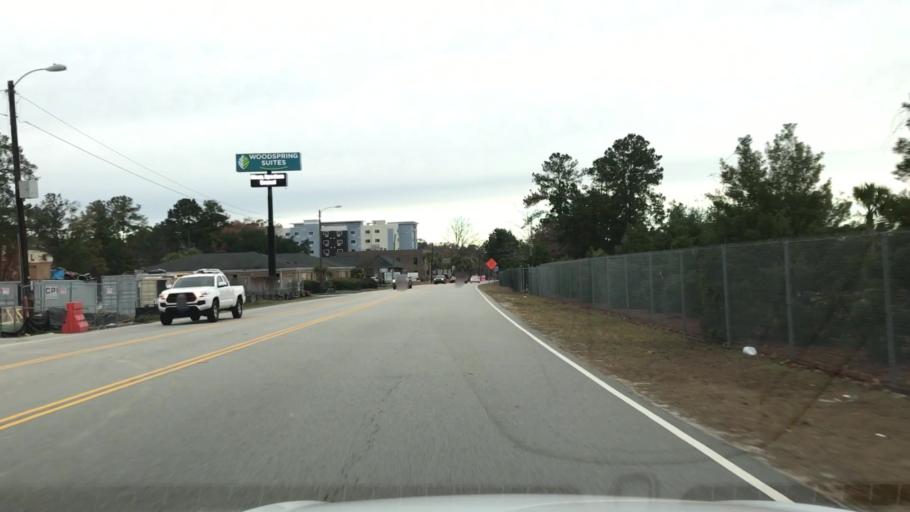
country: US
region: South Carolina
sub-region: Berkeley County
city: Hanahan
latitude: 32.9371
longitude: -80.0507
